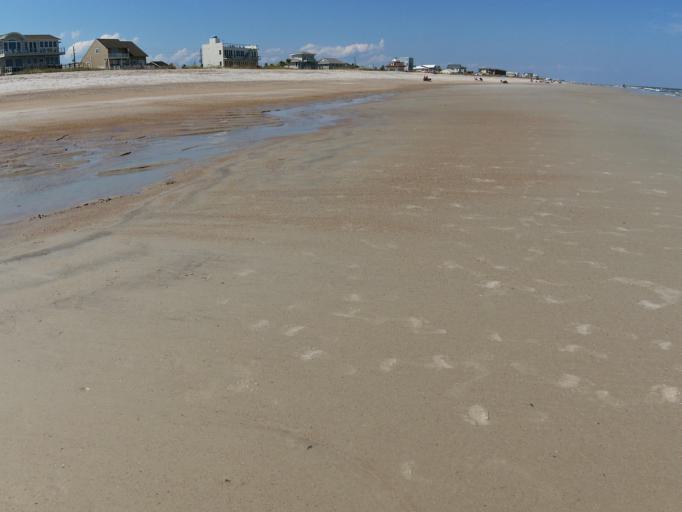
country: US
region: Florida
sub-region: Nassau County
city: Fernandina Beach
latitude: 30.6562
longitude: -81.4318
